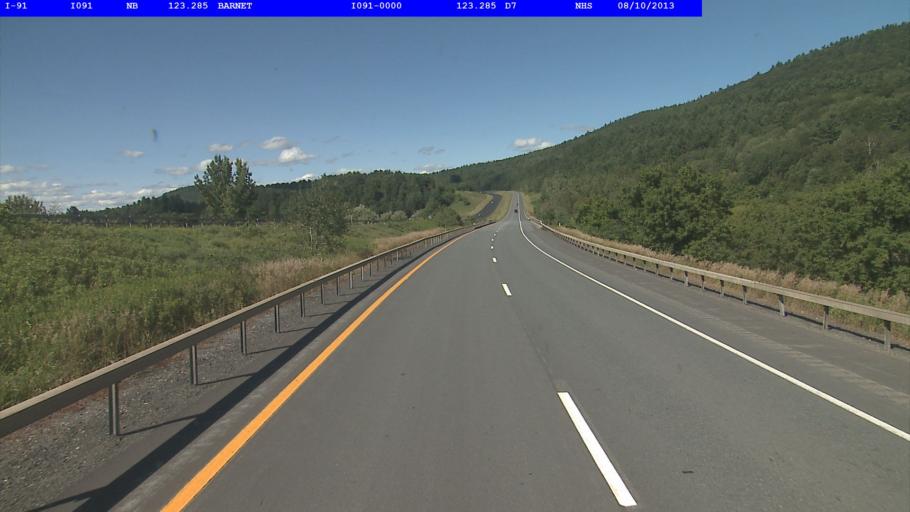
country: US
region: Vermont
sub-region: Caledonia County
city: Saint Johnsbury
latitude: 44.3288
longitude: -72.0388
